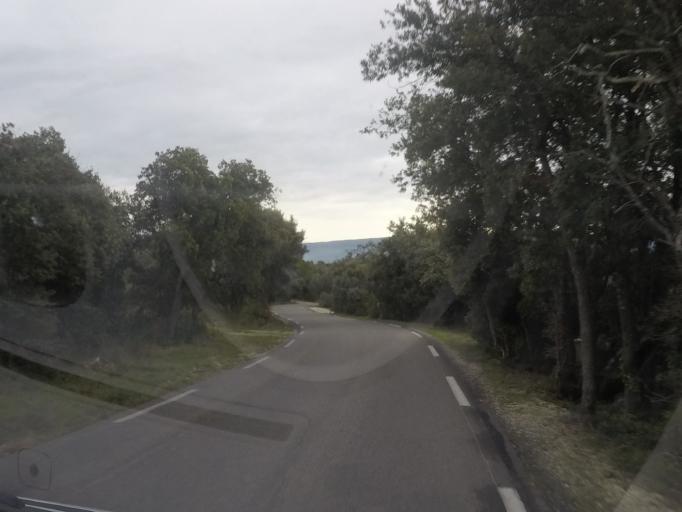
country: FR
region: Provence-Alpes-Cote d'Azur
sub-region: Departement du Vaucluse
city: Gordes
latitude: 43.9199
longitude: 5.1937
